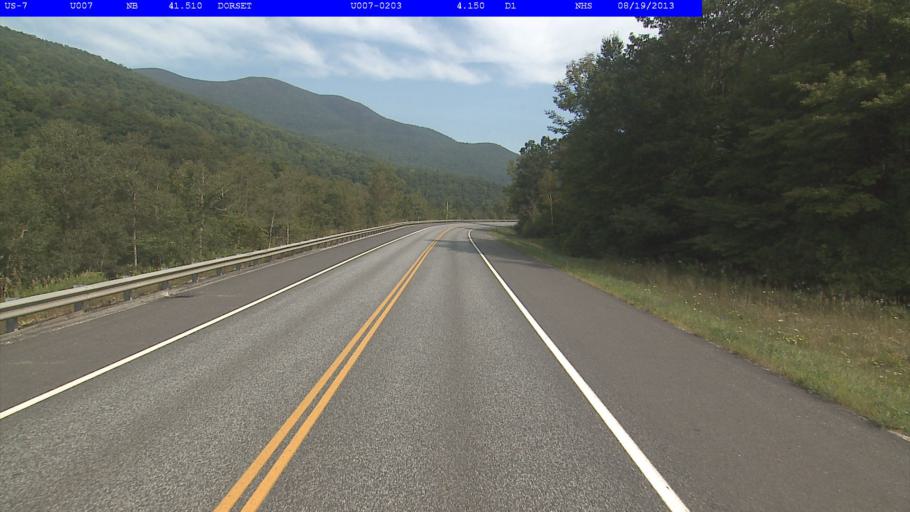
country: US
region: Vermont
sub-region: Bennington County
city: Manchester Center
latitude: 43.2689
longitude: -73.0065
